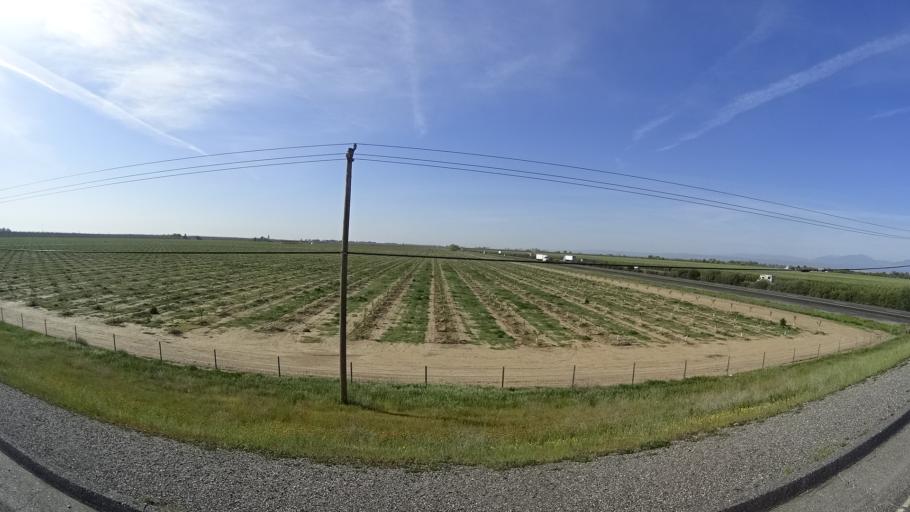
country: US
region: California
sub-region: Glenn County
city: Orland
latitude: 39.6678
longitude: -122.2037
